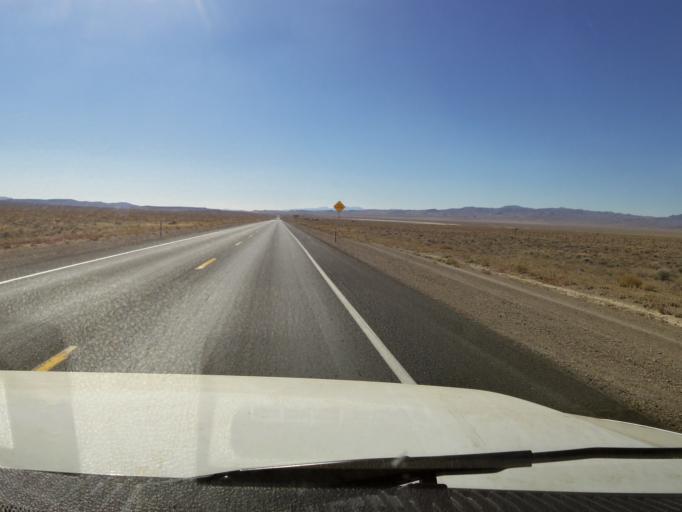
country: US
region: Nevada
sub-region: Esmeralda County
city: Goldfield
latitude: 37.5168
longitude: -117.1887
